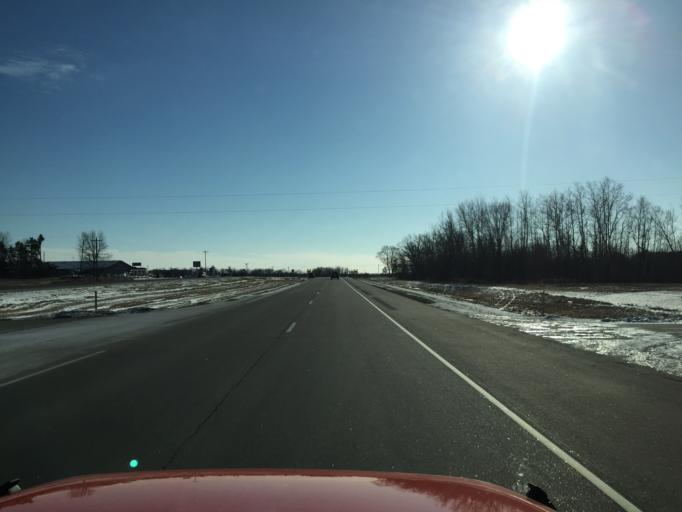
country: US
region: Minnesota
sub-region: Mille Lacs County
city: Milaca
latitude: 45.8271
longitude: -93.6587
